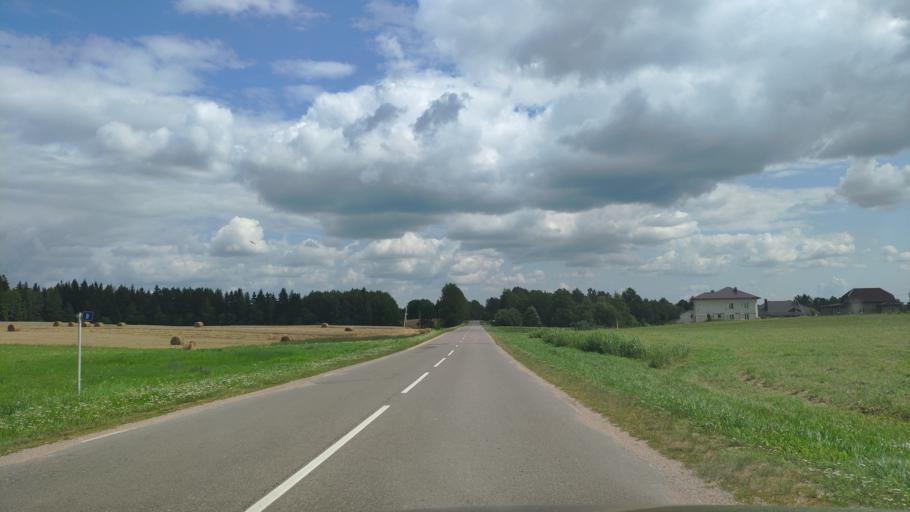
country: BY
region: Minsk
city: Khatsyezhyna
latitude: 53.8809
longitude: 27.2792
